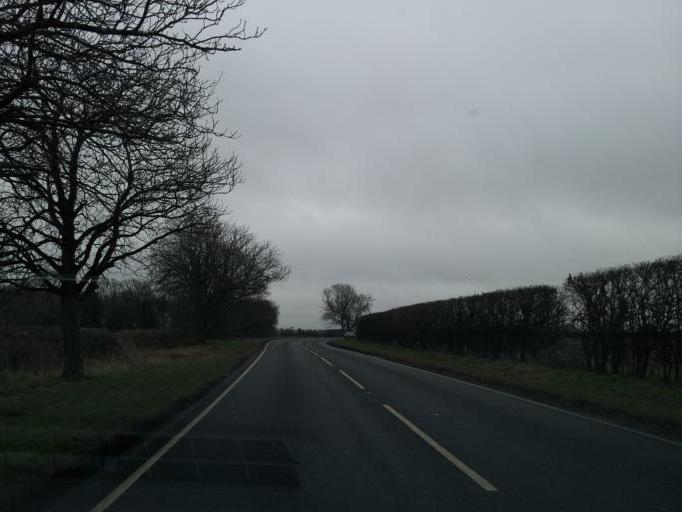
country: GB
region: England
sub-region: Essex
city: Mistley
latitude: 51.9278
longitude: 1.0813
